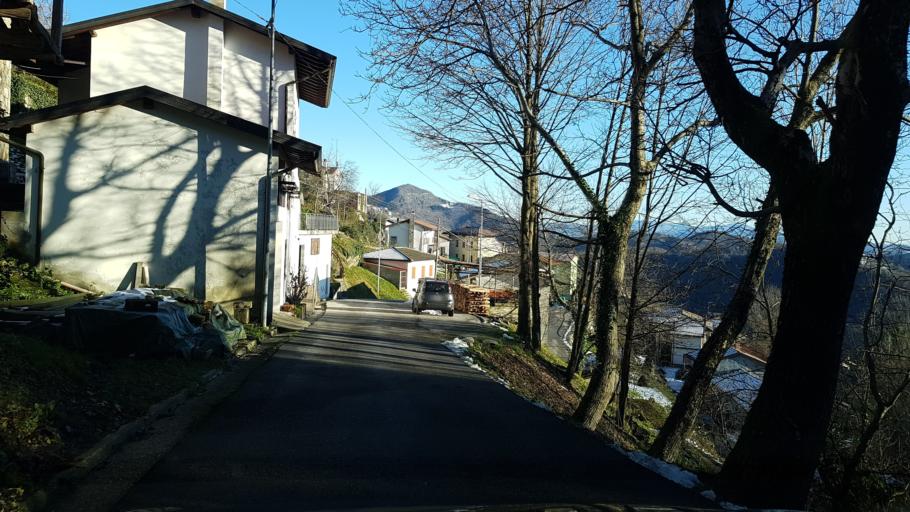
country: IT
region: Friuli Venezia Giulia
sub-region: Provincia di Udine
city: Savogna
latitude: 46.1876
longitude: 13.5311
